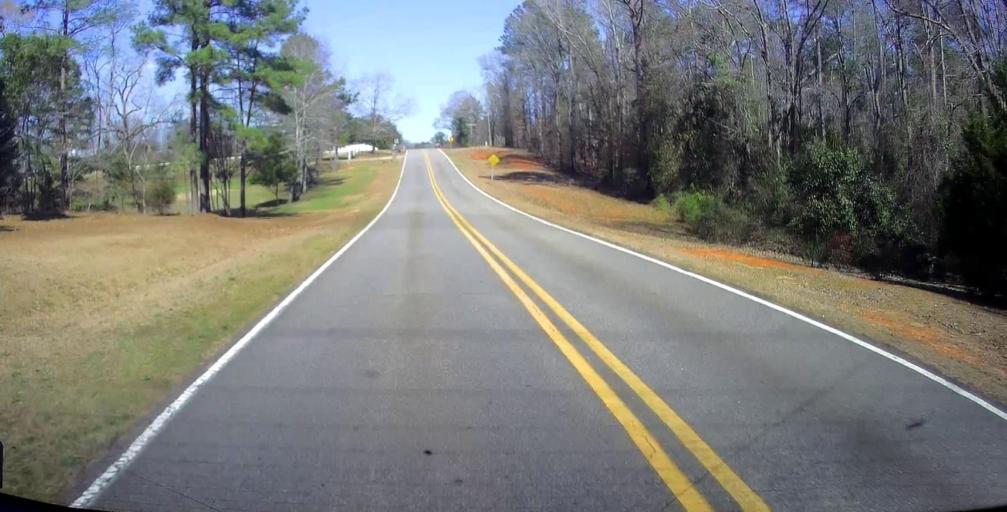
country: US
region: Georgia
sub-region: Houston County
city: Warner Robins
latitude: 32.5613
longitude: -83.6345
